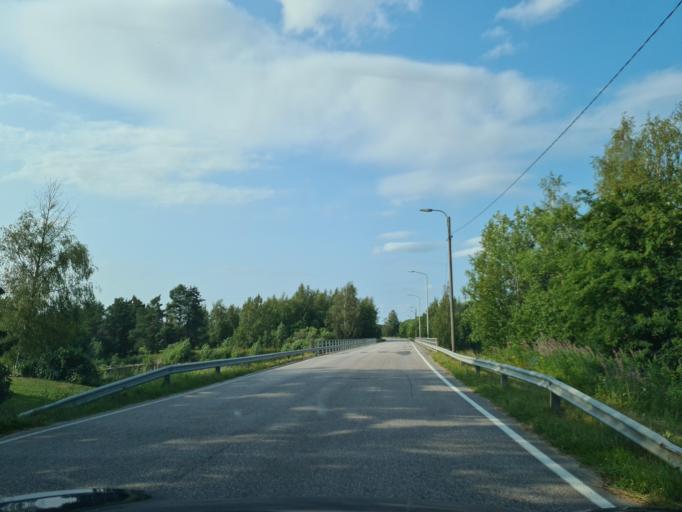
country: FI
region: Ostrobothnia
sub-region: Vaasa
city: Vaehaekyroe
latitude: 63.0077
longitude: 22.1493
